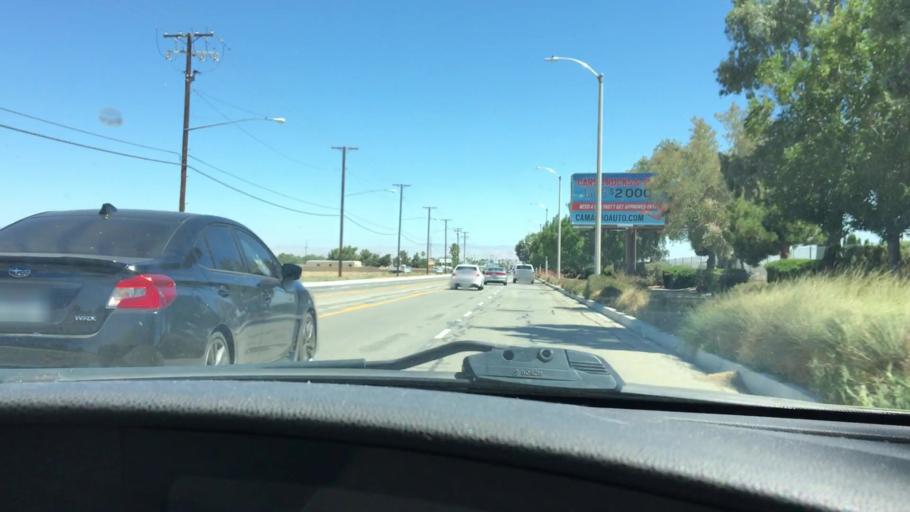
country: US
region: California
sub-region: Los Angeles County
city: Lancaster
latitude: 34.6705
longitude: -118.1321
